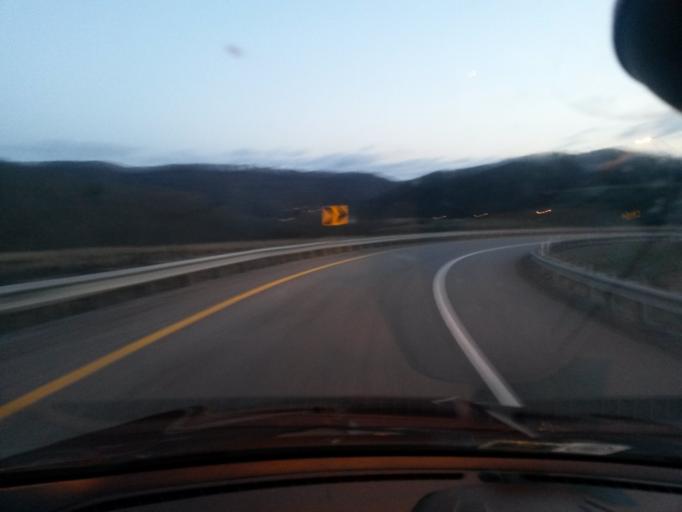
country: US
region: West Virginia
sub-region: Mercer County
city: Bluefield
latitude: 37.2750
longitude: -81.1659
